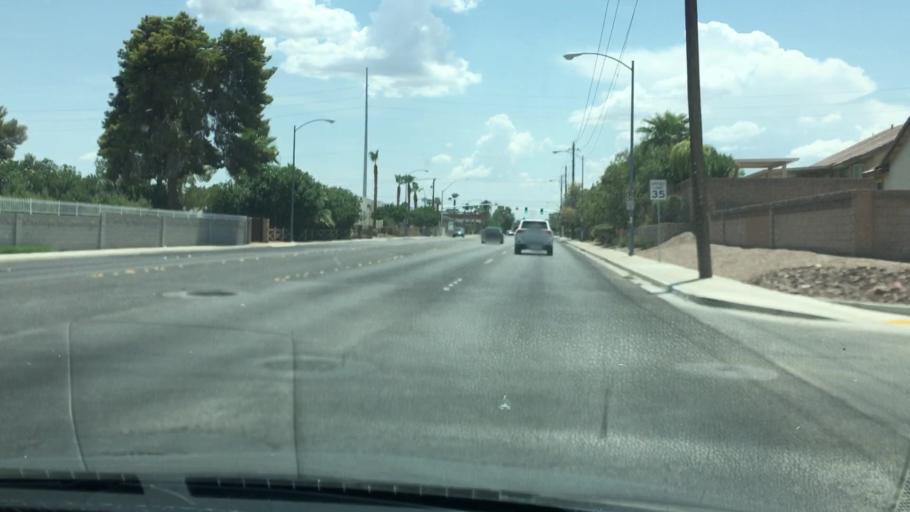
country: US
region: Nevada
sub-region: Clark County
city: Whitney
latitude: 36.0804
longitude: -115.0916
